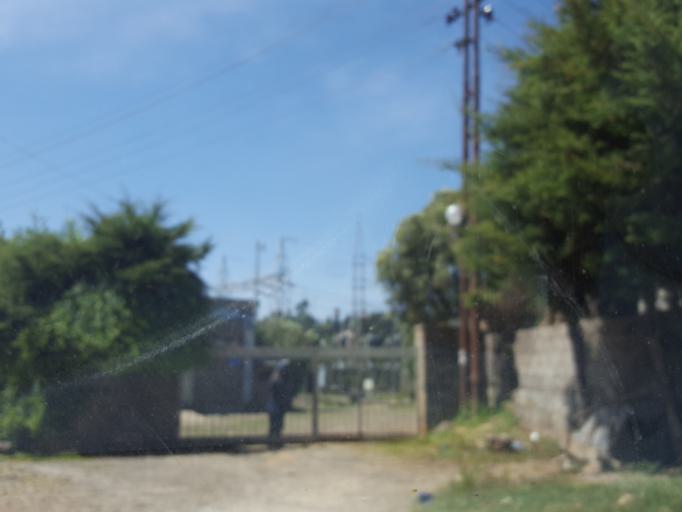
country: ET
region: Adis Abeba
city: Addis Ababa
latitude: 9.0576
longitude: 38.7479
